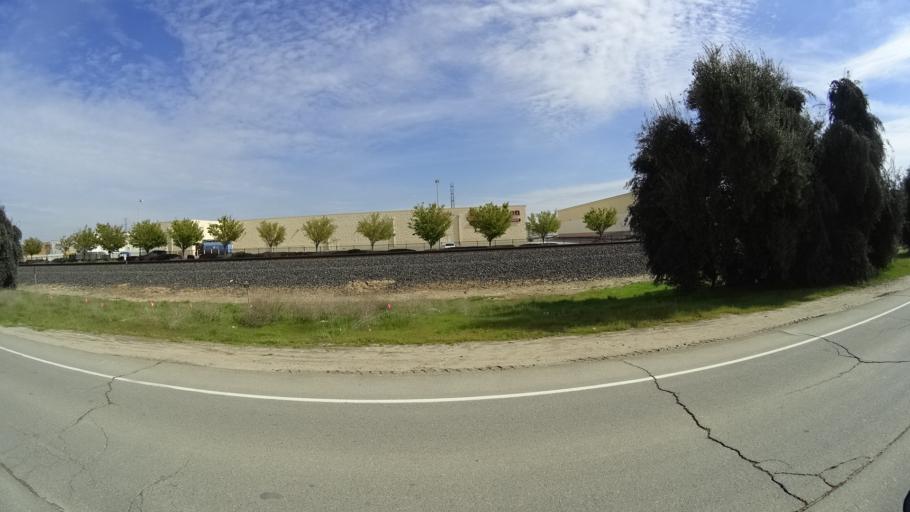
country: US
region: California
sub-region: Fresno County
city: Biola
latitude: 36.8308
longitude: -119.9106
